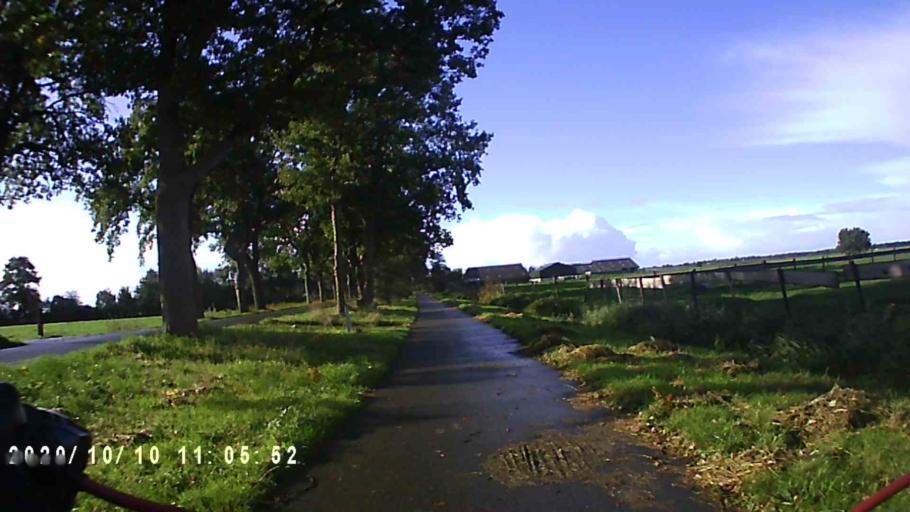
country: NL
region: Friesland
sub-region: Gemeente Achtkarspelen
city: Surhuisterveen
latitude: 53.1276
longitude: 6.2195
